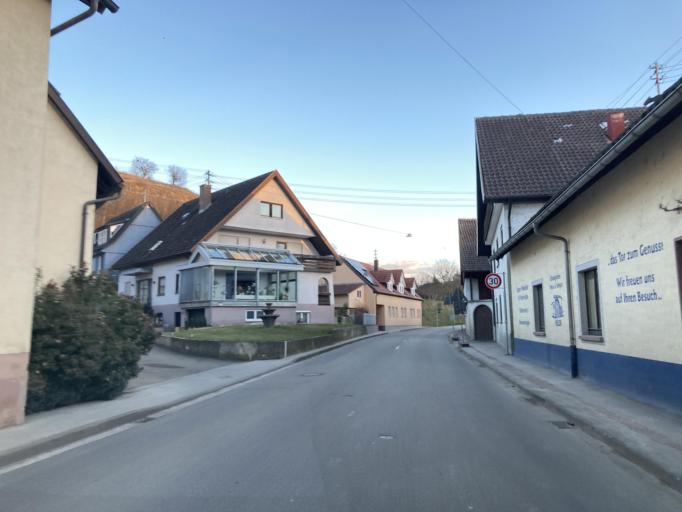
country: DE
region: Baden-Wuerttemberg
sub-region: Freiburg Region
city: Sasbach
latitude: 48.1181
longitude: 7.6098
